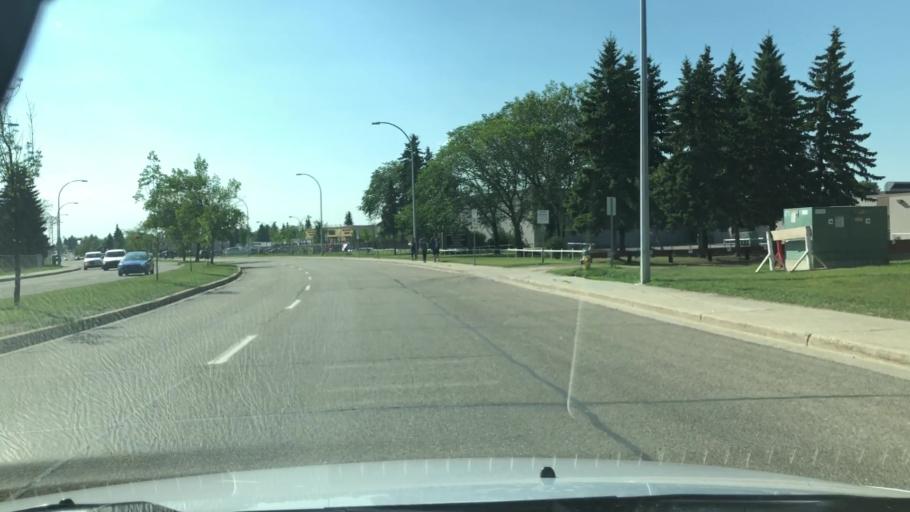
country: CA
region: Alberta
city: Edmonton
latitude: 53.6068
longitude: -113.4549
